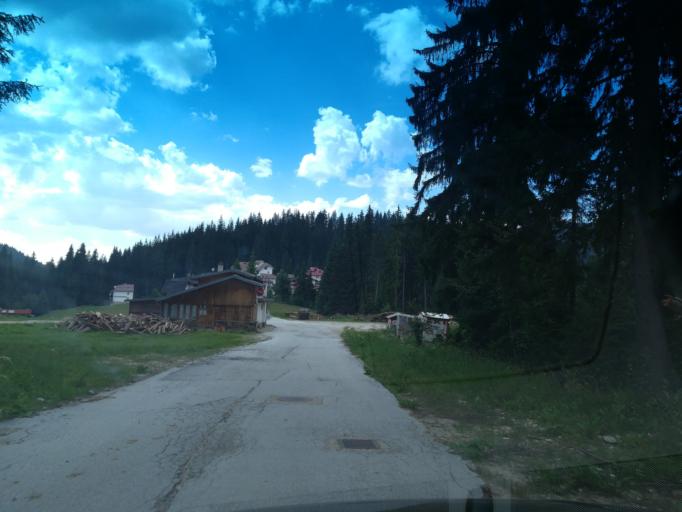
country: BG
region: Smolyan
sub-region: Obshtina Smolyan
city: Smolyan
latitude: 41.6552
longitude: 24.6828
